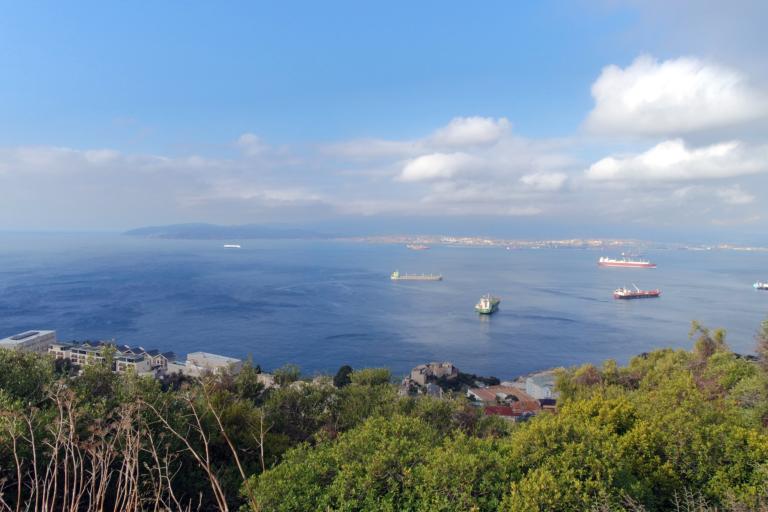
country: GI
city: Gibraltar
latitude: 36.1205
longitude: -5.3457
